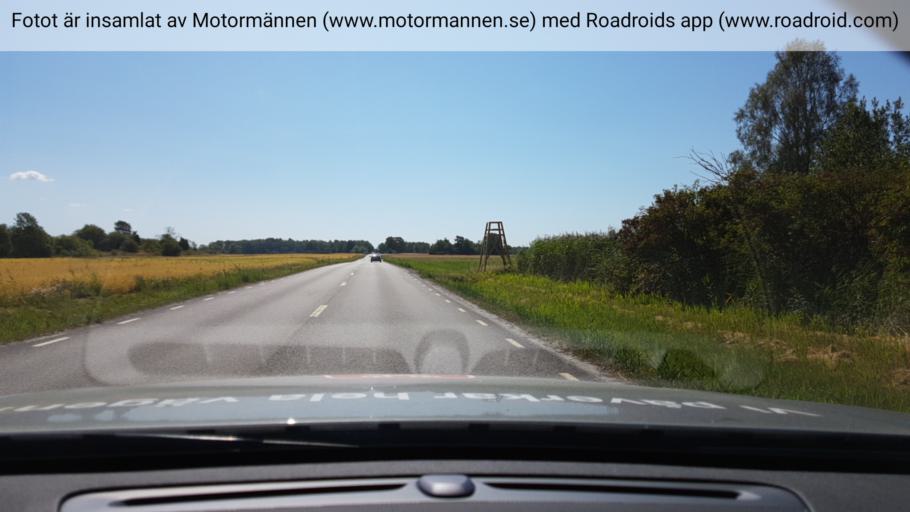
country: SE
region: Stockholm
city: Stenhamra
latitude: 59.3597
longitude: 17.7190
